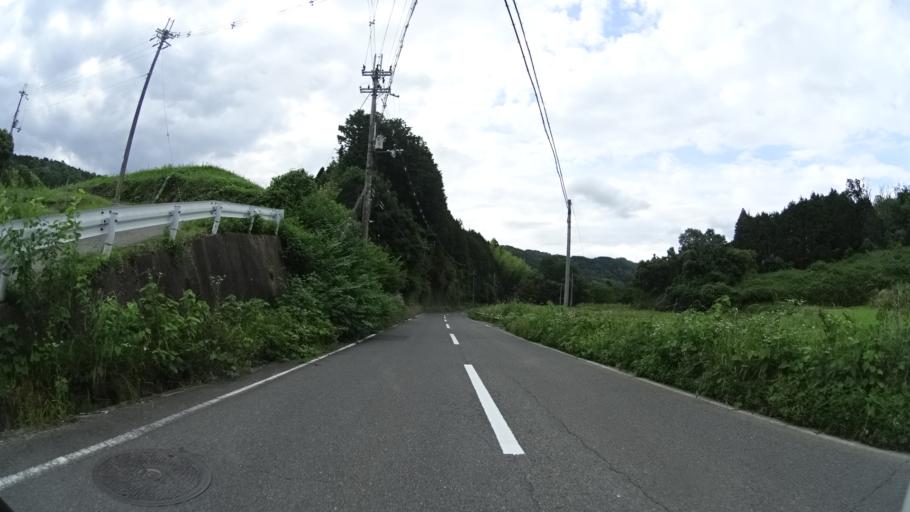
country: JP
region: Nara
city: Nara-shi
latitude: 34.7232
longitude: 135.9097
